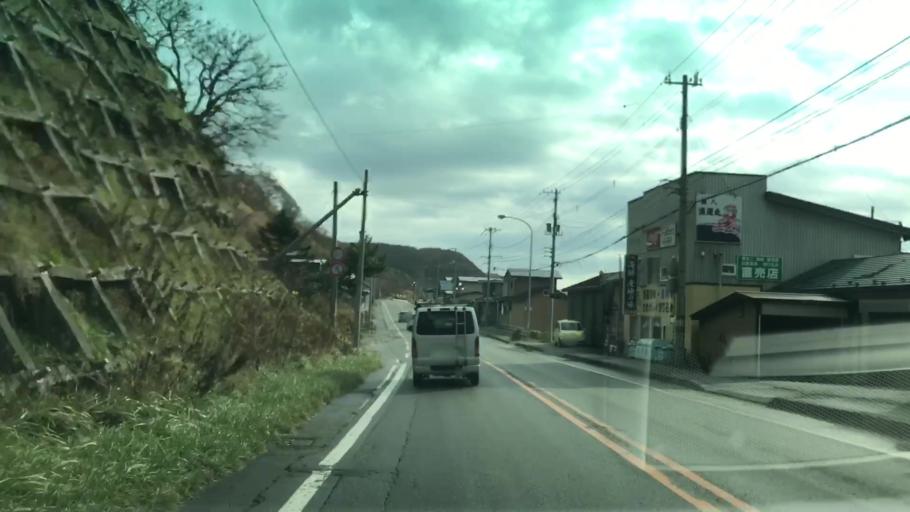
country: JP
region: Hokkaido
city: Shizunai-furukawacho
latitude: 42.1523
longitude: 142.7985
